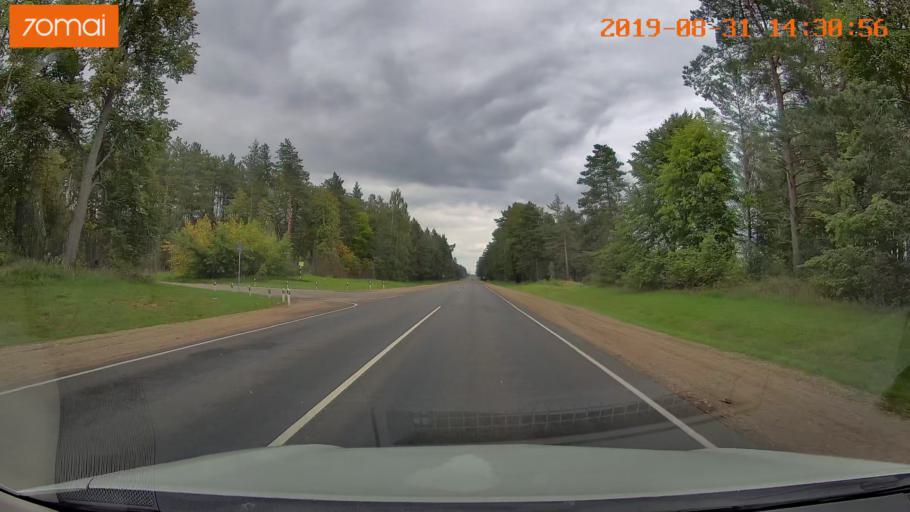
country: RU
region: Smolensk
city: Yekimovichi
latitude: 54.1349
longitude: 33.3623
